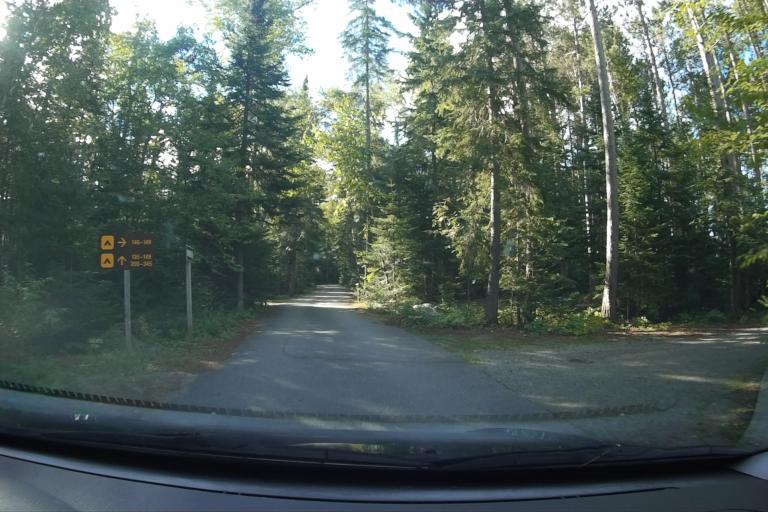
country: CA
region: Ontario
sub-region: Algoma
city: Sault Ste. Marie
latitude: 47.3272
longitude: -84.6112
